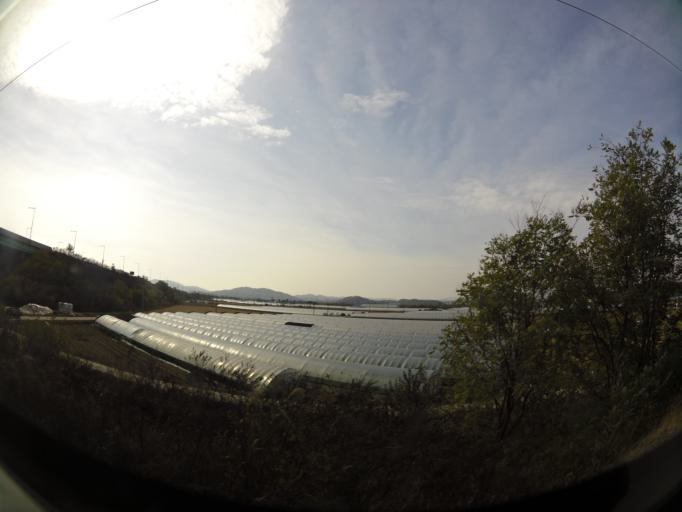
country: KR
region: Daejeon
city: Songgang-dong
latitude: 36.5716
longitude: 127.3147
